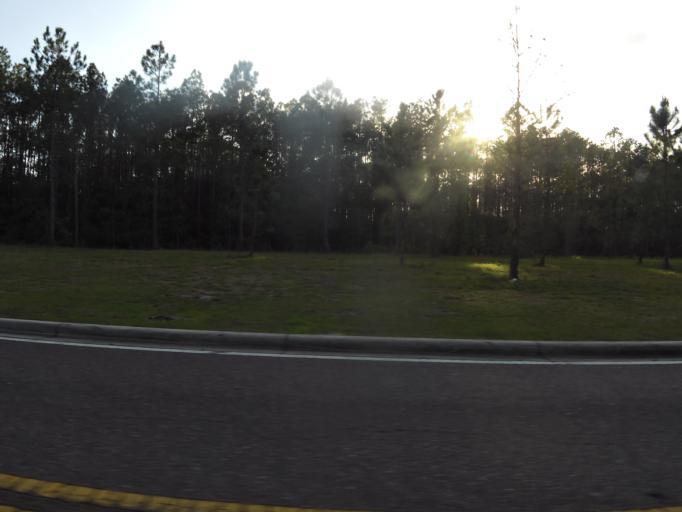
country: US
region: Florida
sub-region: Saint Johns County
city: Fruit Cove
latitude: 30.0834
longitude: -81.5298
